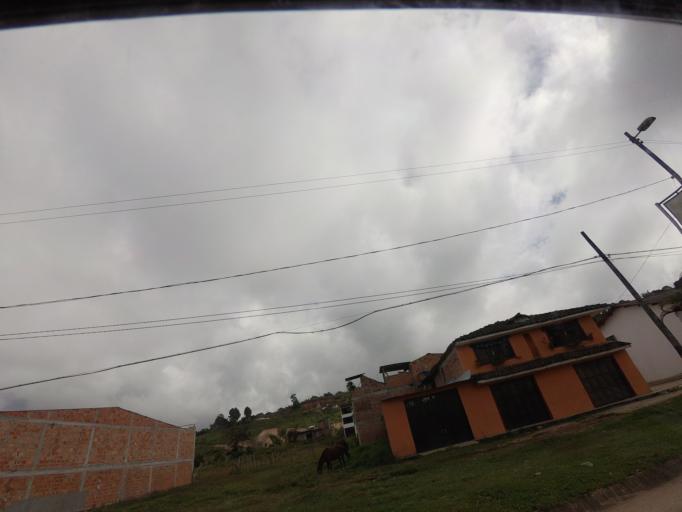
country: CO
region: Huila
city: San Agustin
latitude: 1.8855
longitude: -76.2753
